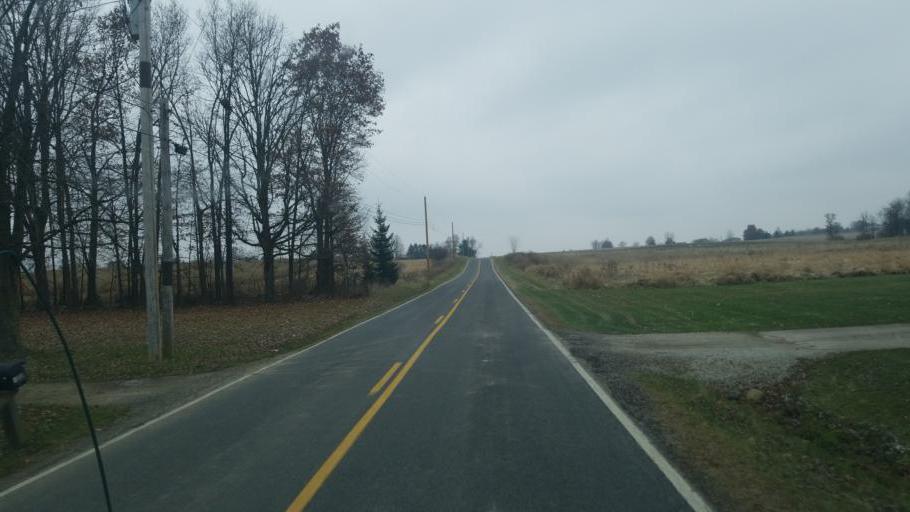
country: US
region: Ohio
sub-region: Medina County
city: Lodi
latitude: 41.1297
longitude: -82.0020
